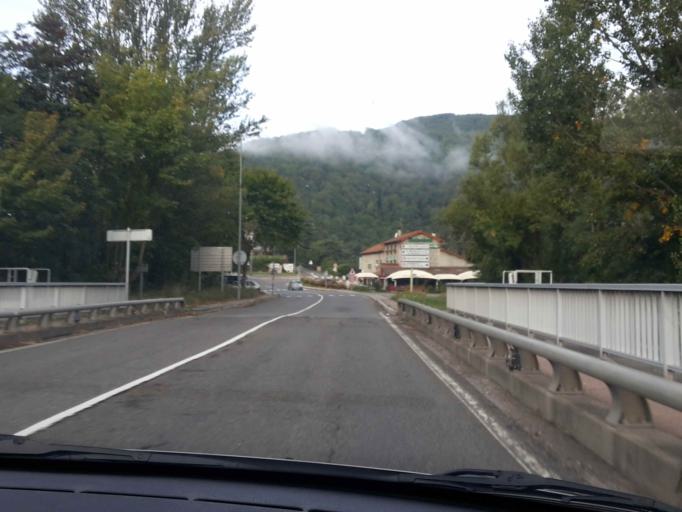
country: FR
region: Rhone-Alpes
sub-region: Departement de la Loire
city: Saint-Paul-en-Cornillon
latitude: 45.4086
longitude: 4.2476
